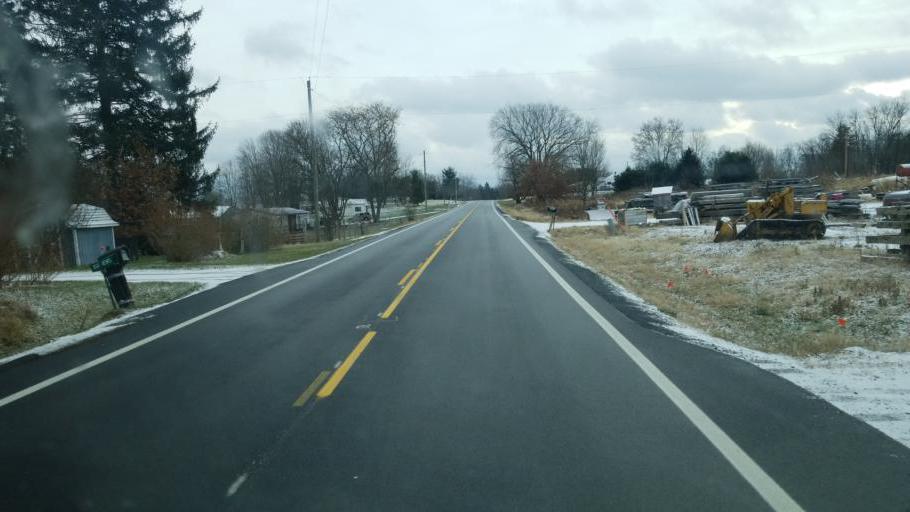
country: US
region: Ohio
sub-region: Knox County
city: Gambier
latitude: 40.3502
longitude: -82.4389
